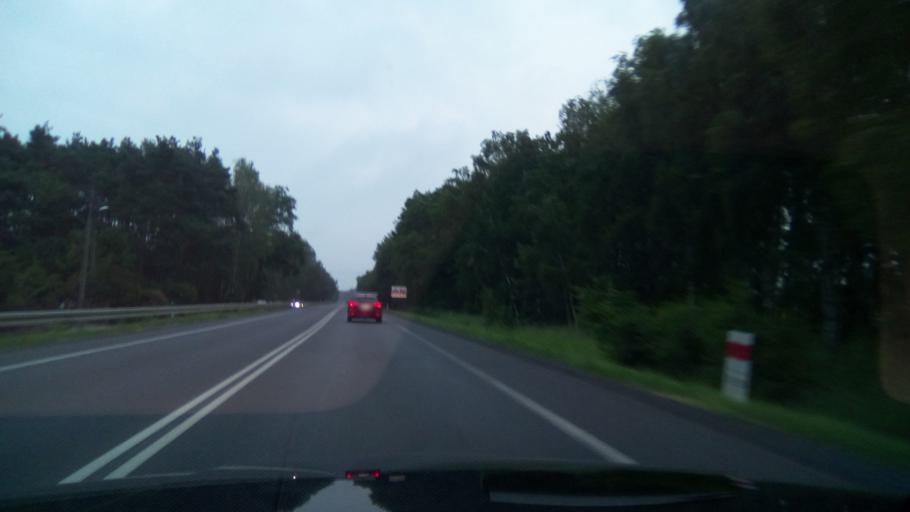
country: PL
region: Greater Poland Voivodeship
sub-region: Powiat poznanski
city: Kostrzyn
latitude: 52.4687
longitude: 17.1786
